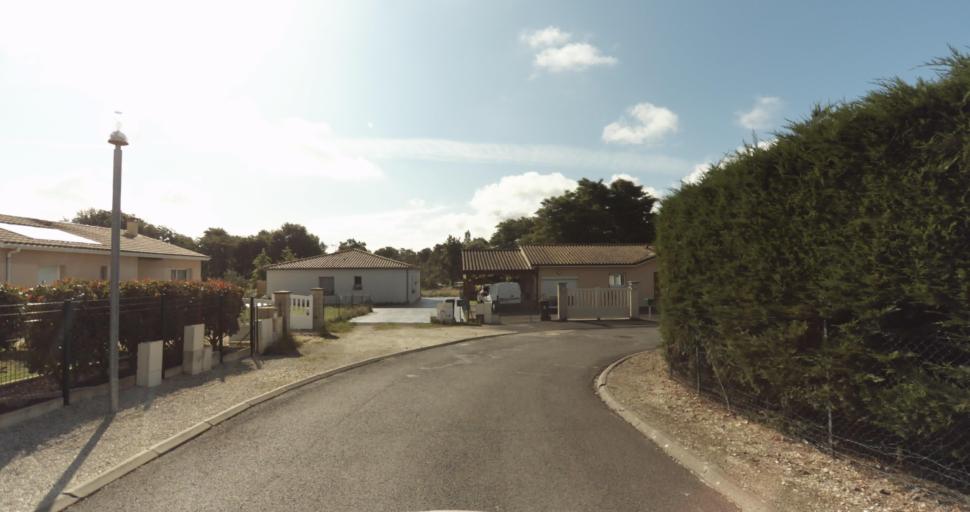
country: FR
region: Aquitaine
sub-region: Departement de la Gironde
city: Bazas
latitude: 44.4331
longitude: -0.2437
